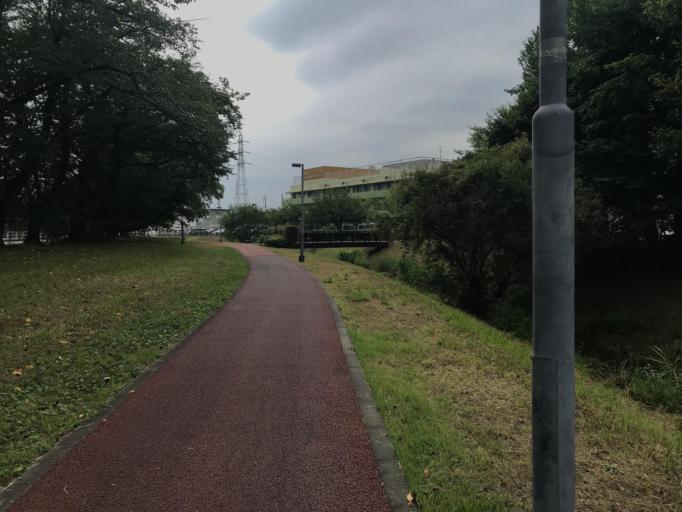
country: JP
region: Tokyo
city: Higashimurayama-shi
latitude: 35.7529
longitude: 139.4959
